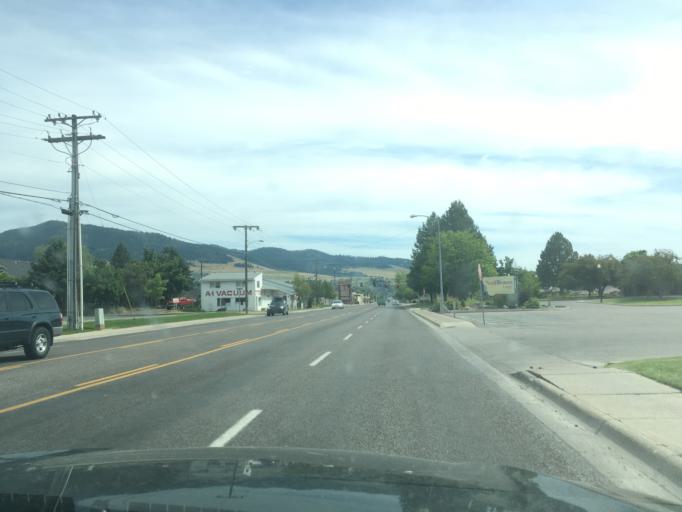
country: US
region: Montana
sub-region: Missoula County
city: Missoula
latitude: 46.8550
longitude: -114.0183
